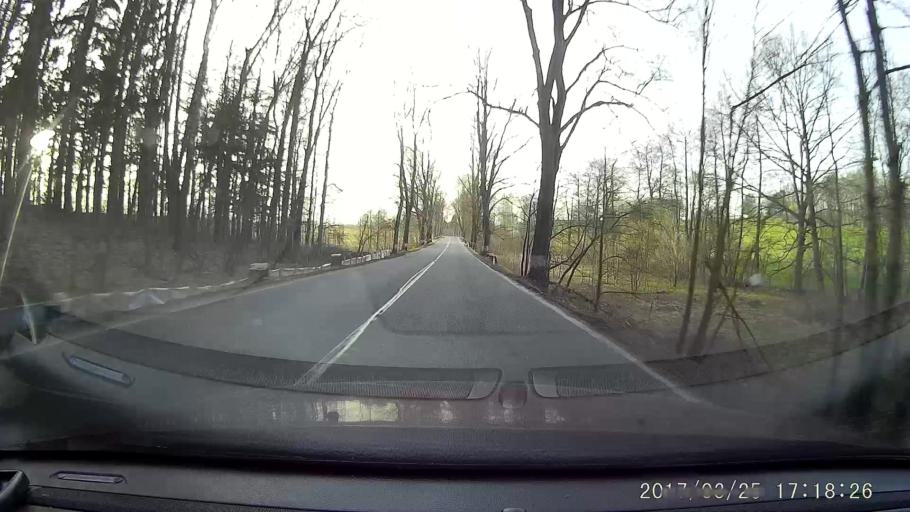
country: CZ
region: Liberecky
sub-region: Okres Liberec
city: Frydlant
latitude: 50.9750
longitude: 15.0829
